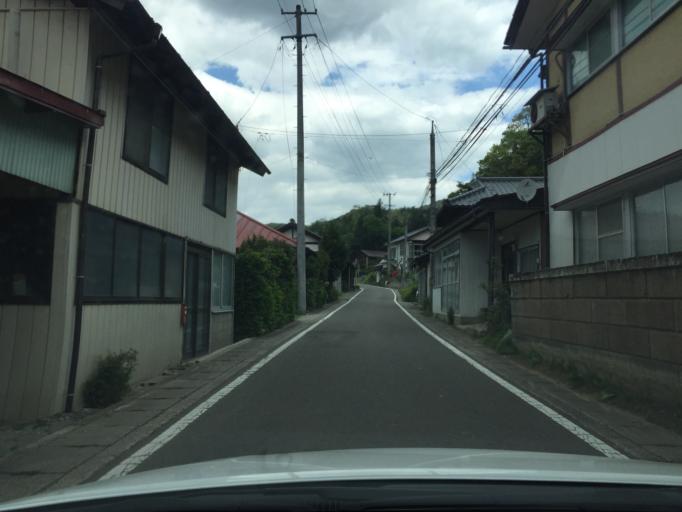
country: JP
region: Fukushima
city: Fukushima-shi
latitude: 37.6971
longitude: 140.5585
